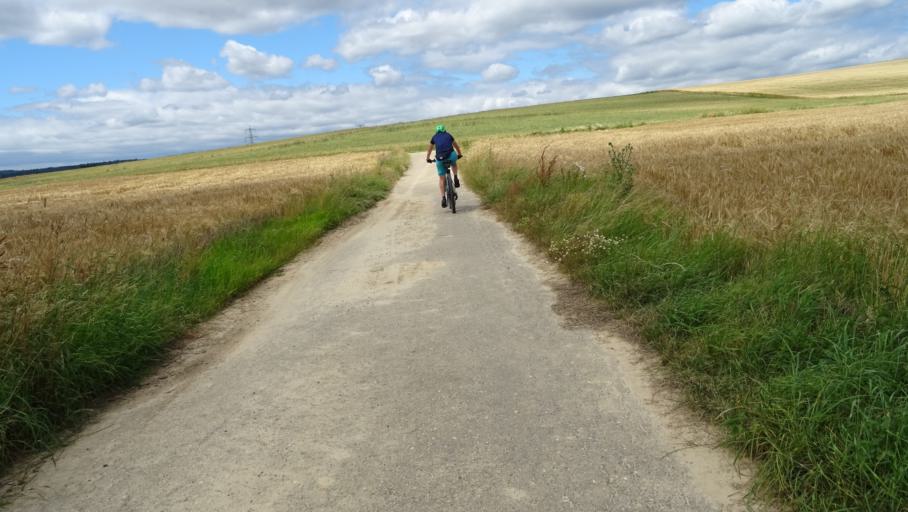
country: DE
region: Baden-Wuerttemberg
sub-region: Karlsruhe Region
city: Neunkirchen
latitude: 49.3758
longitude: 9.0312
